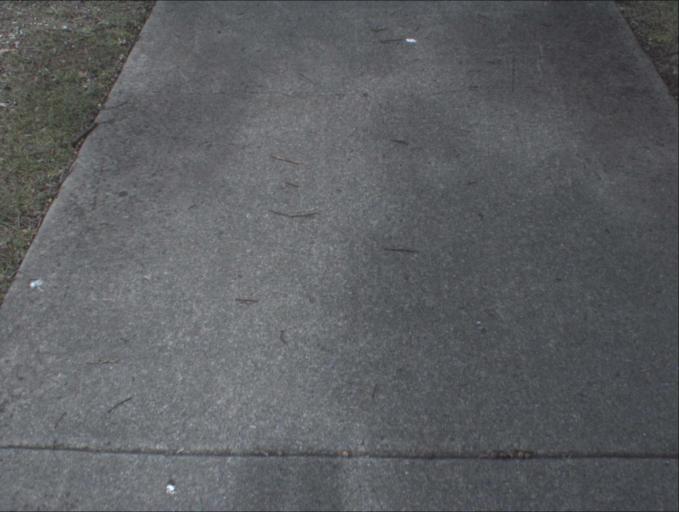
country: AU
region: Queensland
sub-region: Logan
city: Waterford West
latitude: -27.6966
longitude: 153.1354
